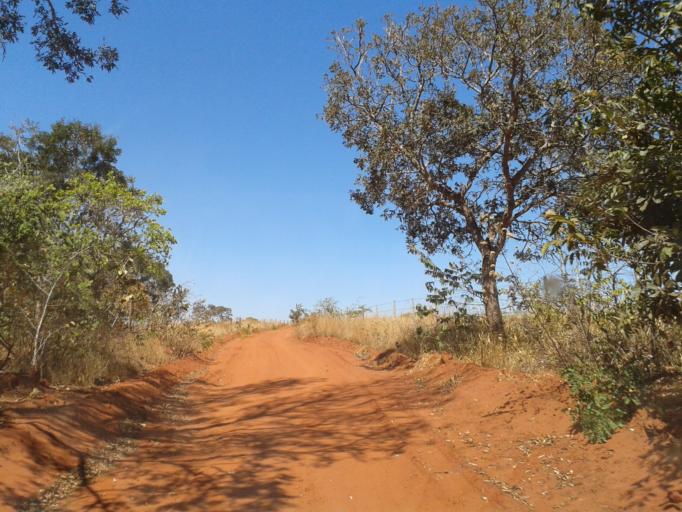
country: BR
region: Minas Gerais
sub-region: Ituiutaba
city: Ituiutaba
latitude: -19.1001
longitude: -49.2703
